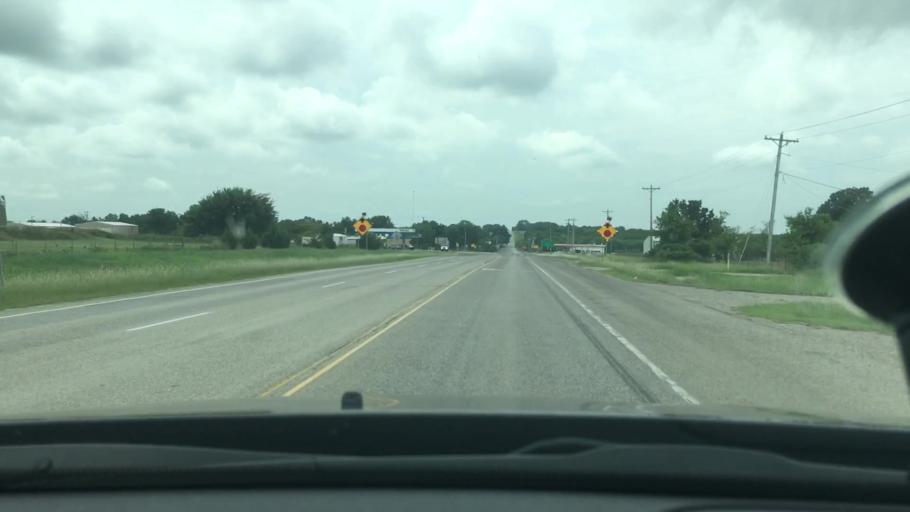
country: US
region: Oklahoma
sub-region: Carter County
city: Wilson
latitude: 34.1764
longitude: -97.4749
